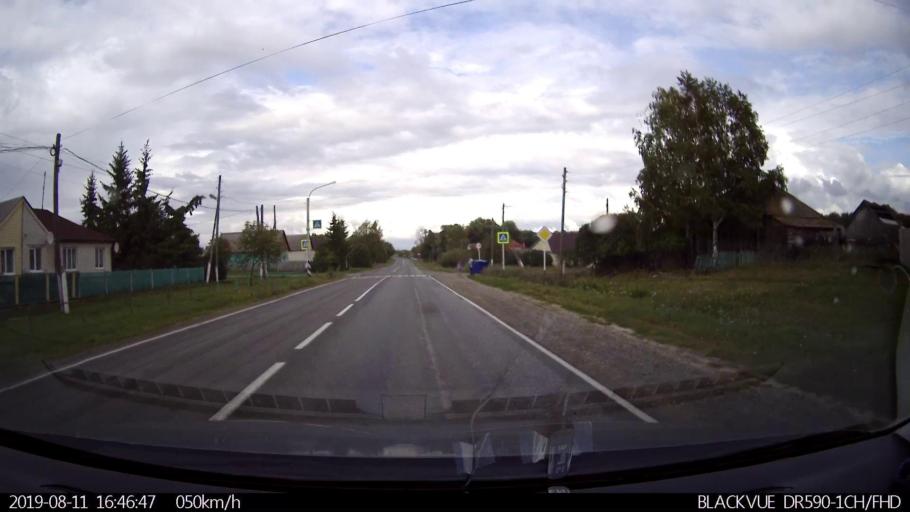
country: RU
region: Ulyanovsk
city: Mayna
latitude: 54.1997
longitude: 47.6917
